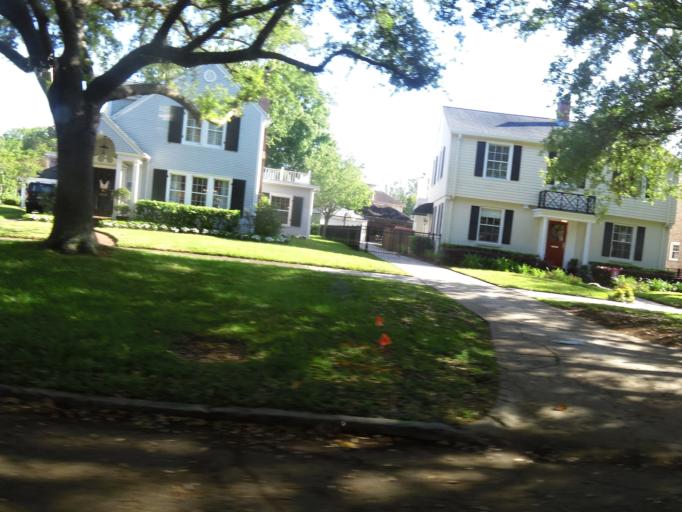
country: US
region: Florida
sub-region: Duval County
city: Jacksonville
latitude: 30.3030
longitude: -81.6554
